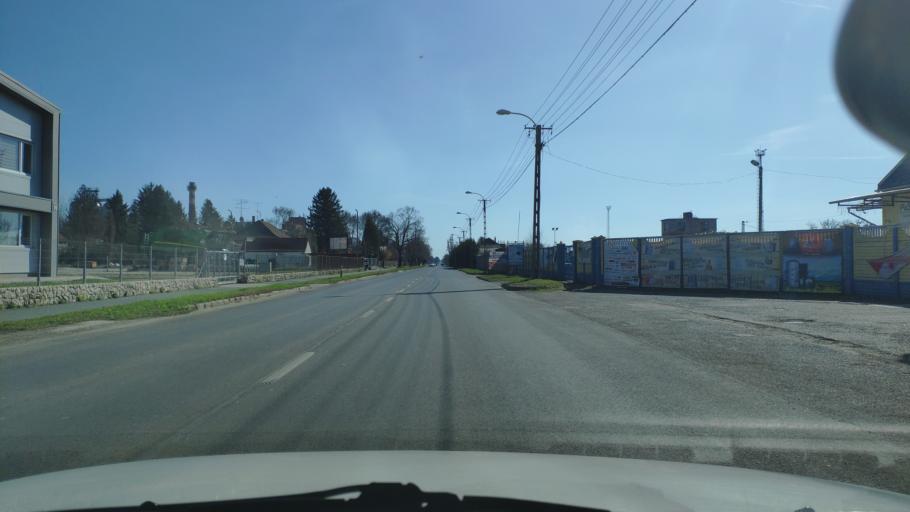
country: HU
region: Zala
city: Nagykanizsa
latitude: 46.4411
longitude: 16.9891
